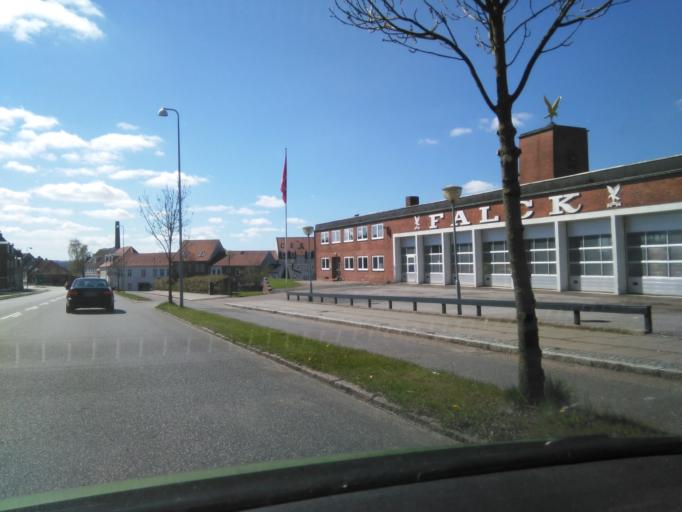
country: DK
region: Central Jutland
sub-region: Horsens Kommune
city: Horsens
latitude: 55.8713
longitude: 9.8441
